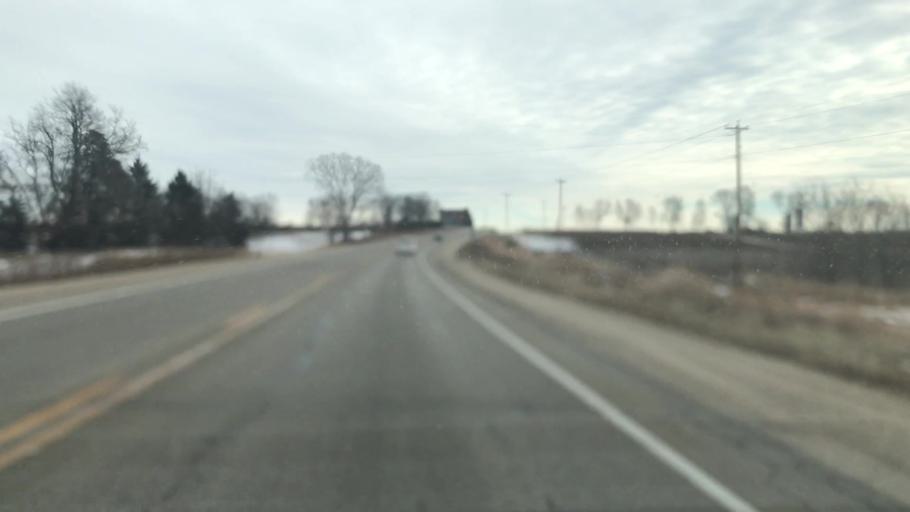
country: US
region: Wisconsin
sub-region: Dodge County
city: Theresa
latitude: 43.4308
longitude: -88.4484
